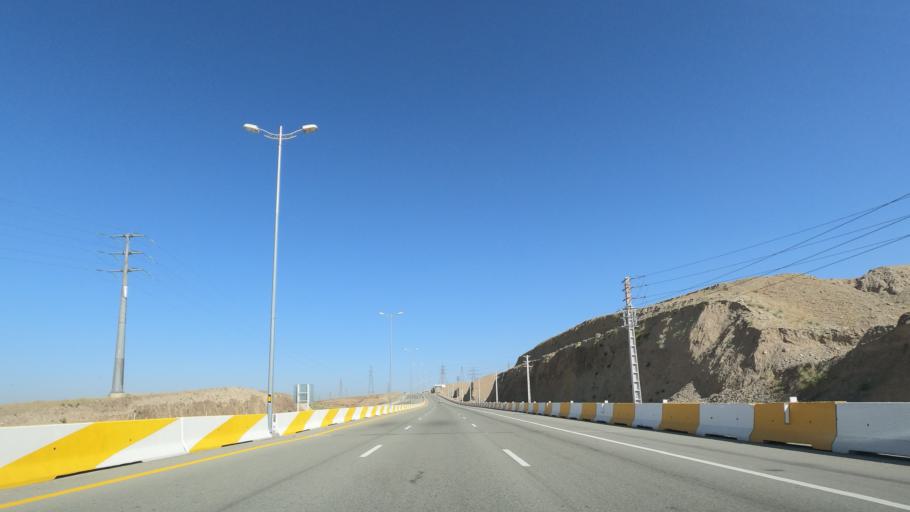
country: IR
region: Tehran
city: Shahr-e Qods
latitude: 35.7709
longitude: 51.0599
